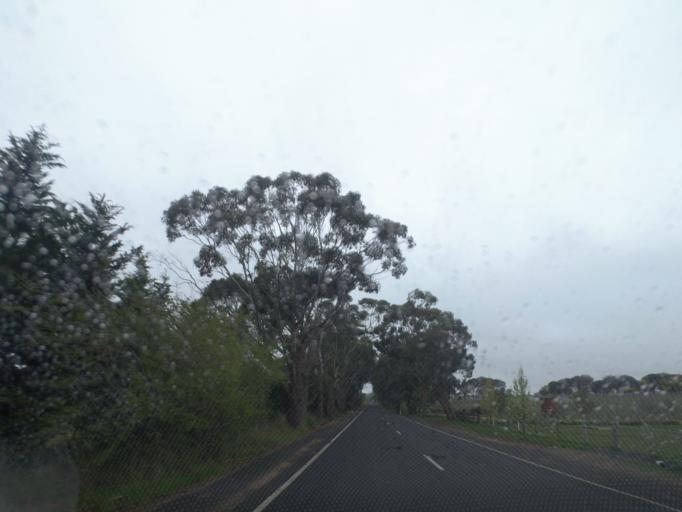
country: AU
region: Victoria
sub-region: Hume
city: Sunbury
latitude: -37.3482
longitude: 144.6260
